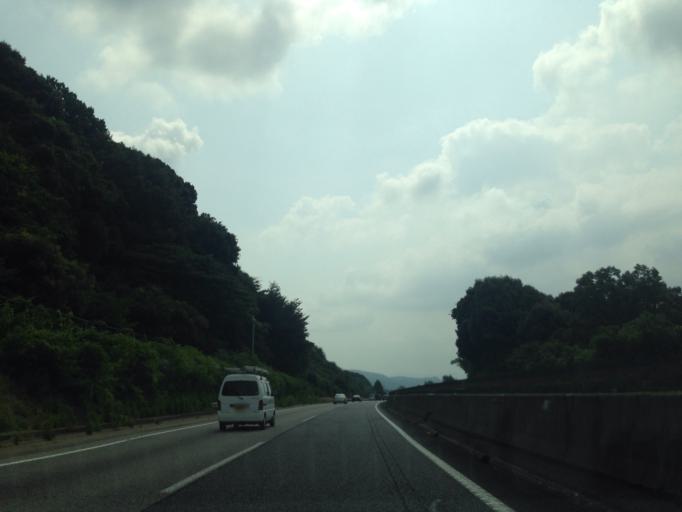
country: JP
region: Aichi
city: Gamagori
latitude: 34.8753
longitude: 137.2816
